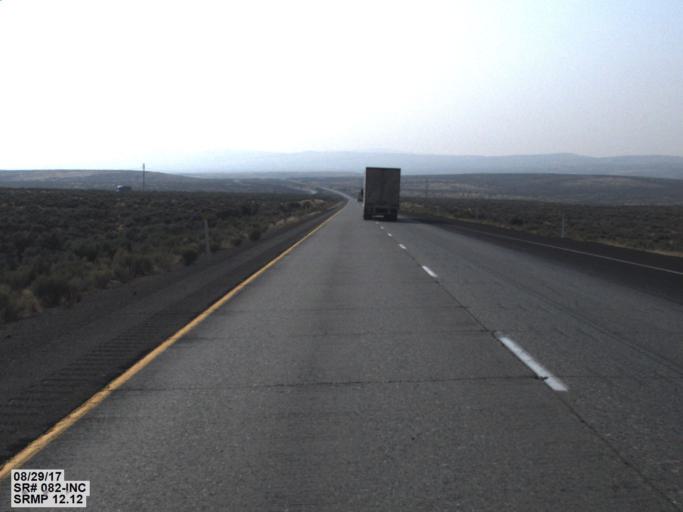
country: US
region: Washington
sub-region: Kittitas County
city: Kittitas
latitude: 46.8379
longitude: -120.3725
